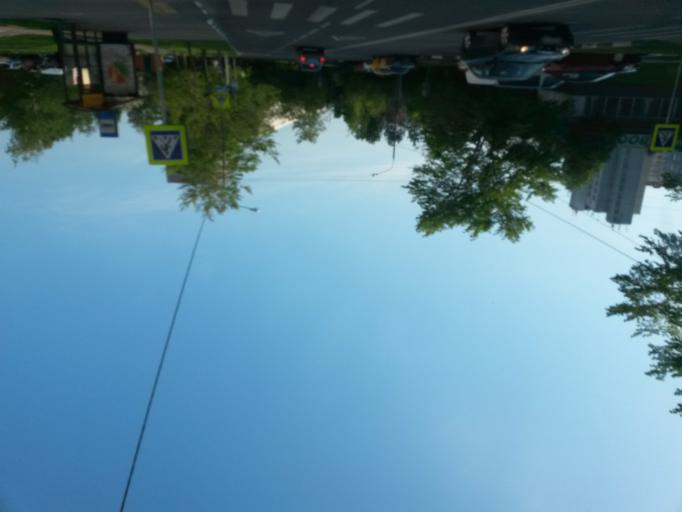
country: RU
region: Moskovskaya
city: Biryulevo Zapadnoye
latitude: 55.5893
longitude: 37.6456
